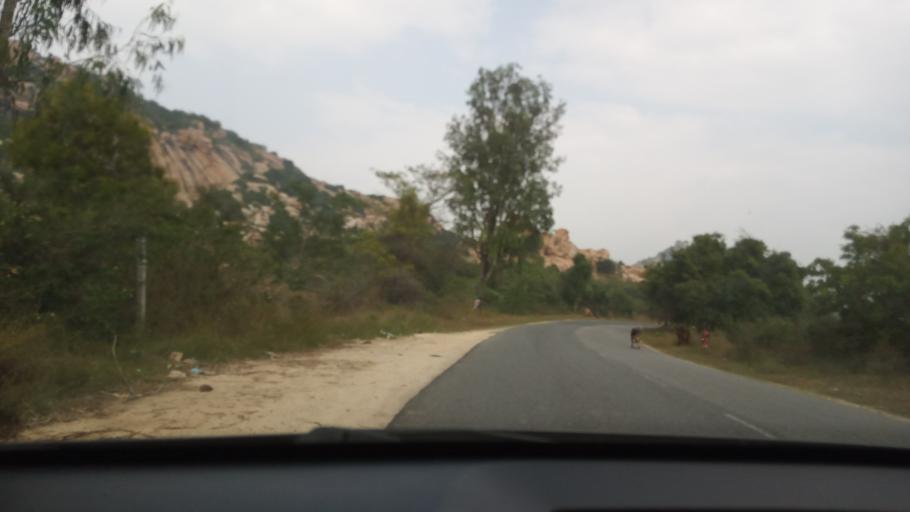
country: IN
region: Andhra Pradesh
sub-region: Chittoor
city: Pakala
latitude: 13.6578
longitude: 78.8605
